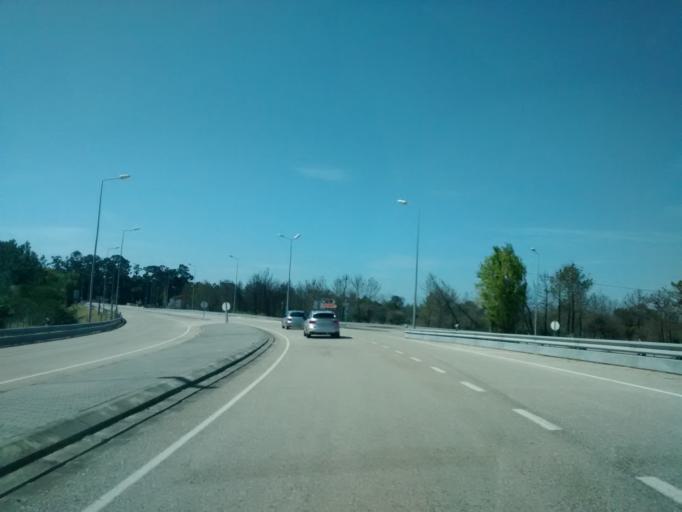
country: PT
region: Coimbra
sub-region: Mira
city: Mira
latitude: 40.4495
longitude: -8.7585
